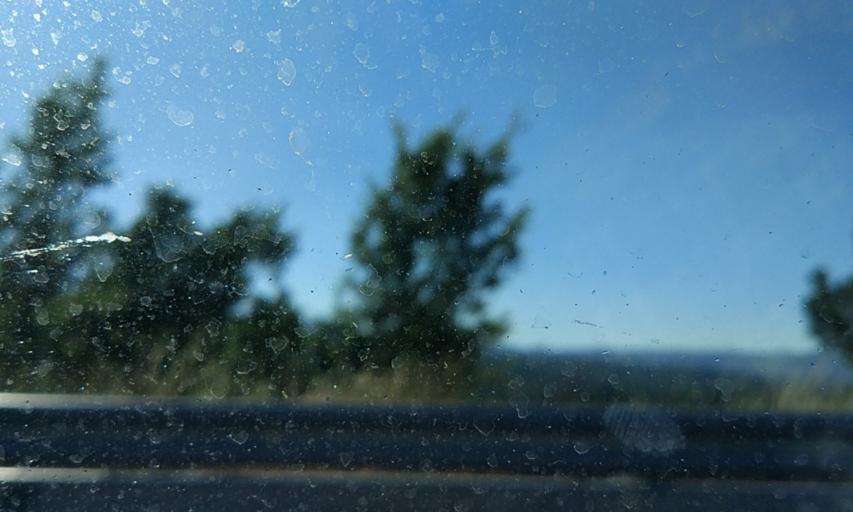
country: PT
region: Vila Real
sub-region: Sabrosa
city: Sabrosa
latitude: 41.3554
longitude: -7.5899
